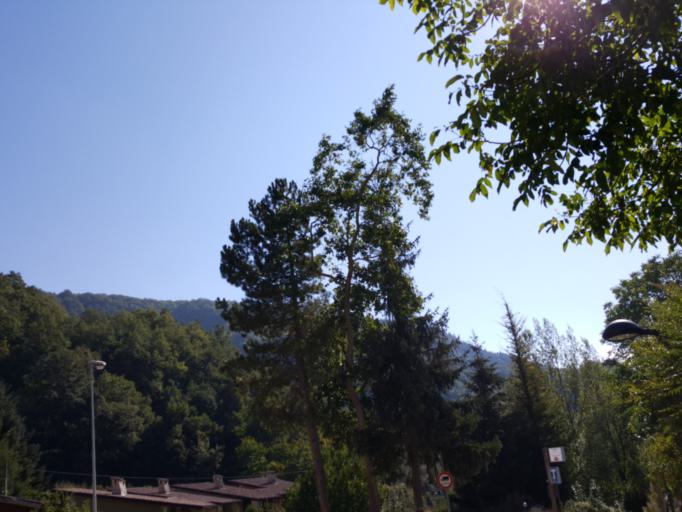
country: IT
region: The Marches
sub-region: Provincia di Ascoli Piceno
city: Arquata del Tronto
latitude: 42.7973
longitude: 13.3018
